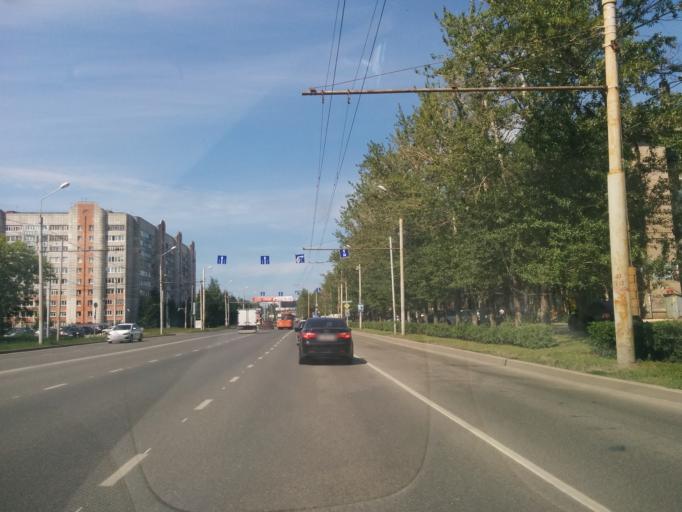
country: RU
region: Perm
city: Perm
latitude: 57.9965
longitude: 56.2877
